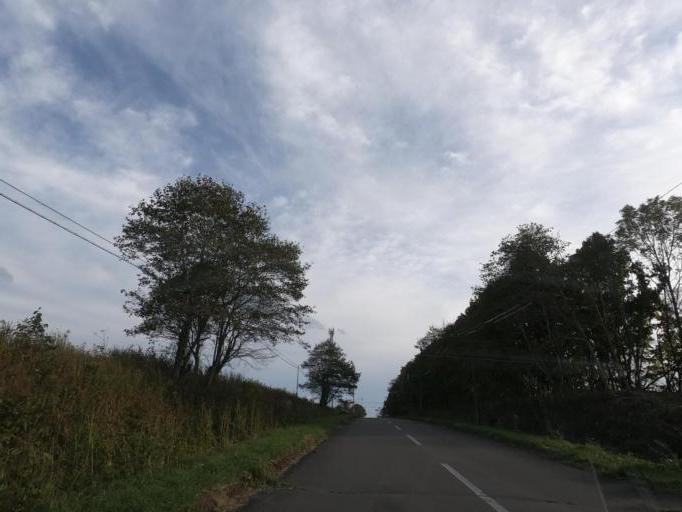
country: JP
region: Hokkaido
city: Obihiro
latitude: 42.5008
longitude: 143.4171
